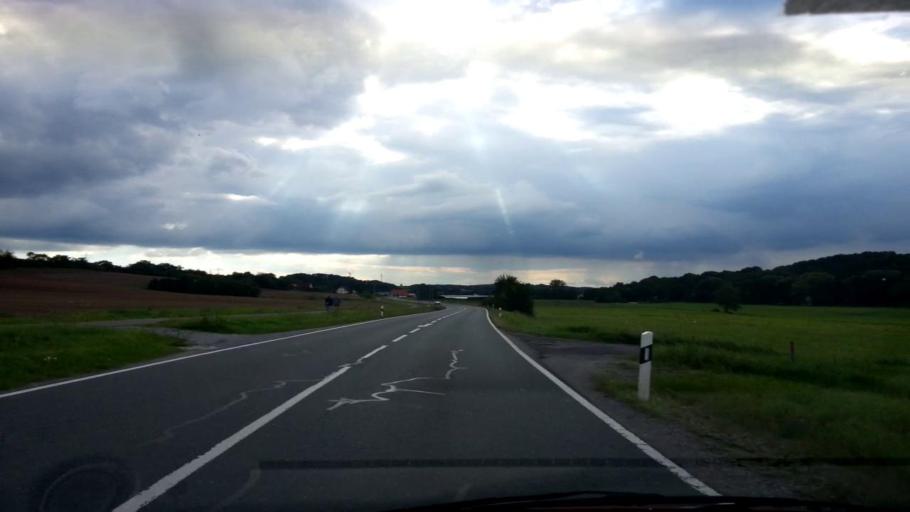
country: DE
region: Bavaria
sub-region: Upper Franconia
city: Schlusselfeld
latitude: 49.7355
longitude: 10.6286
